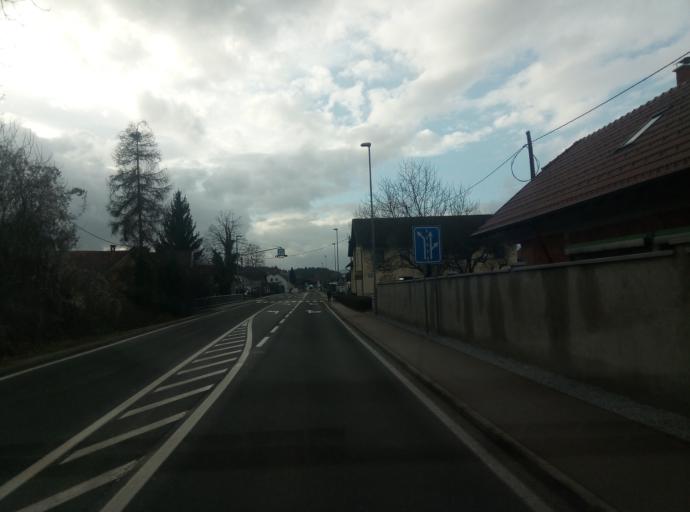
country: SI
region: Lukovica
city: Lukovica pri Domzalah
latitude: 46.1630
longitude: 14.6758
